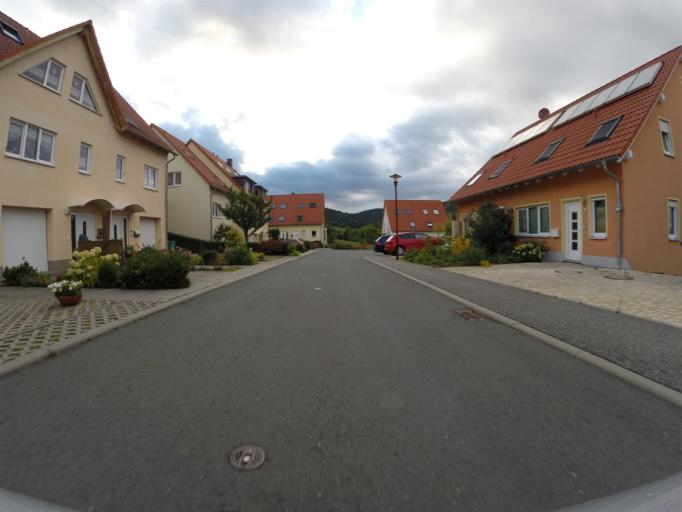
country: DE
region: Thuringia
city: Jena
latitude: 50.9026
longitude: 11.5679
